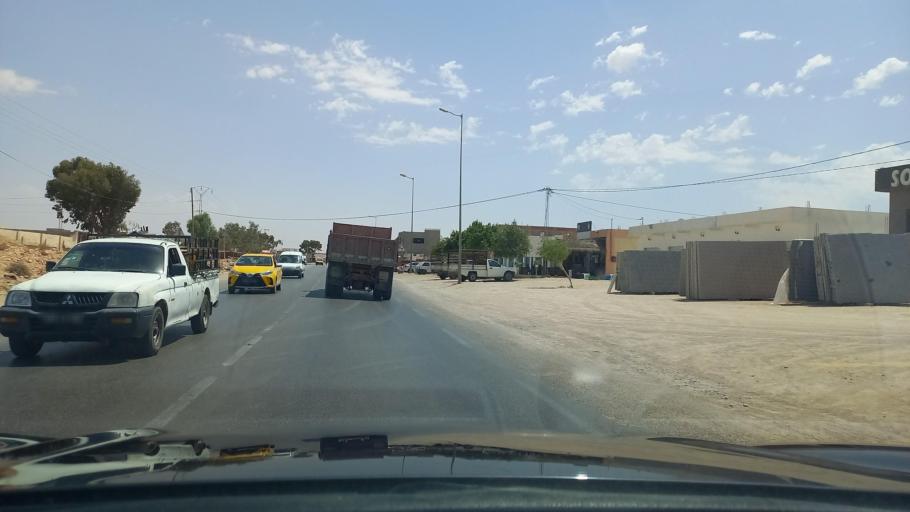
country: TN
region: Madanin
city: Medenine
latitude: 33.3708
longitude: 10.4484
